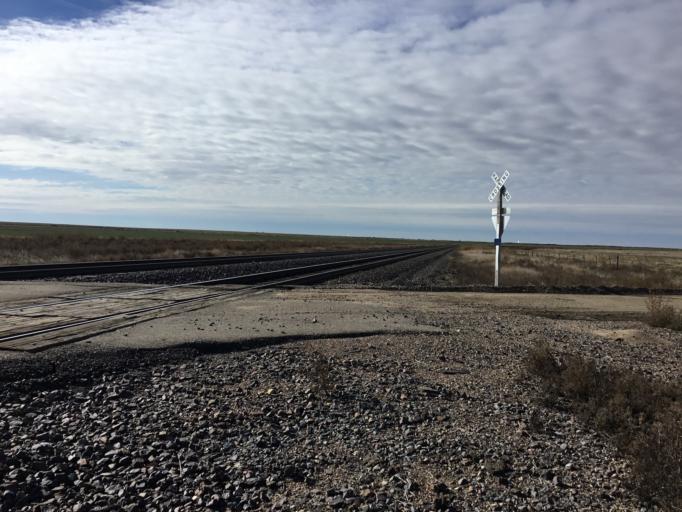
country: US
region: Kansas
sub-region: Trego County
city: WaKeeney
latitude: 39.0309
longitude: -100.1232
